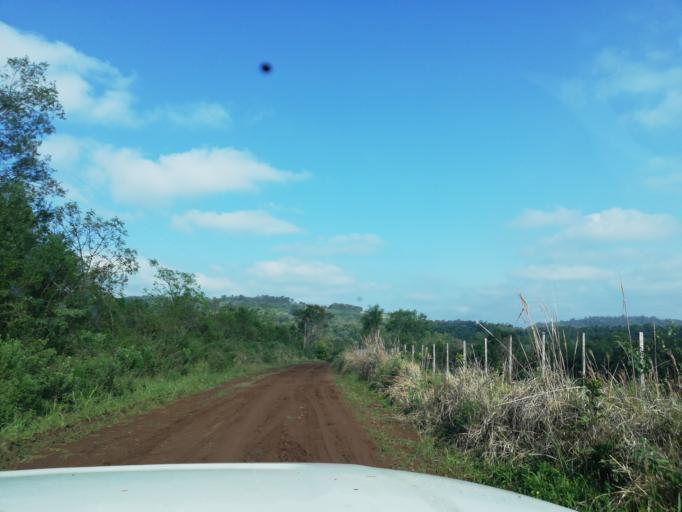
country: AR
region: Misiones
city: Cerro Azul
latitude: -27.5999
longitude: -55.5288
